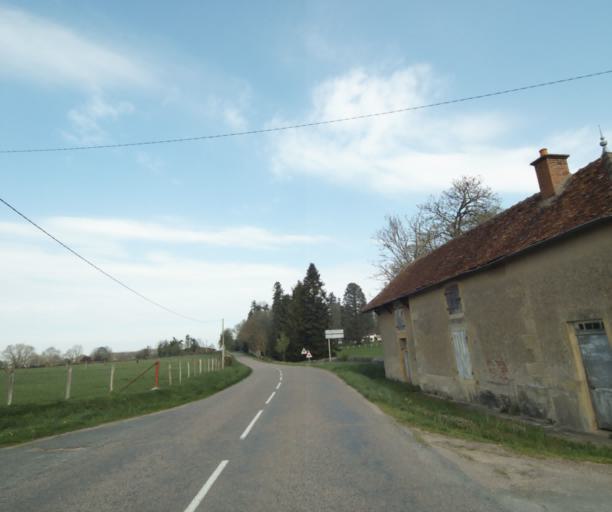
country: FR
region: Bourgogne
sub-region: Departement de Saone-et-Loire
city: Palinges
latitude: 46.5007
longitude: 4.2110
